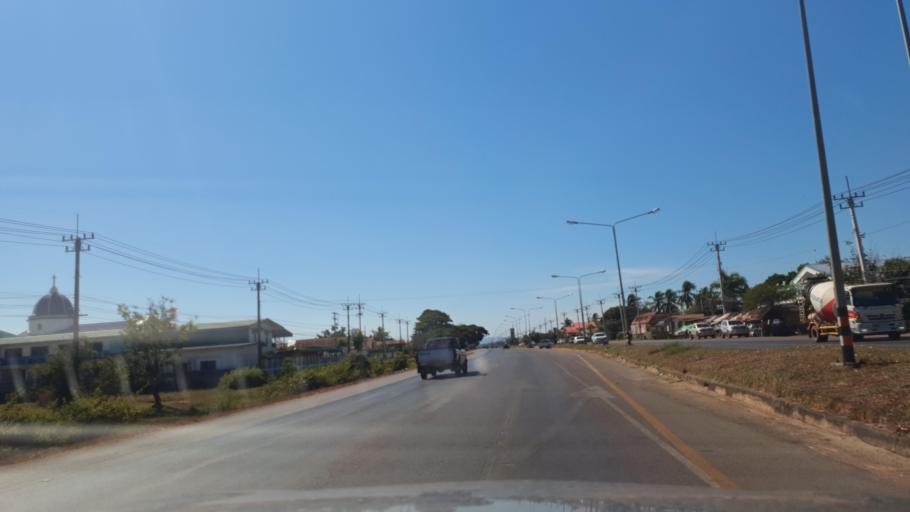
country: TH
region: Sakon Nakhon
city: Sakon Nakhon
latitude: 17.2520
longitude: 104.1138
